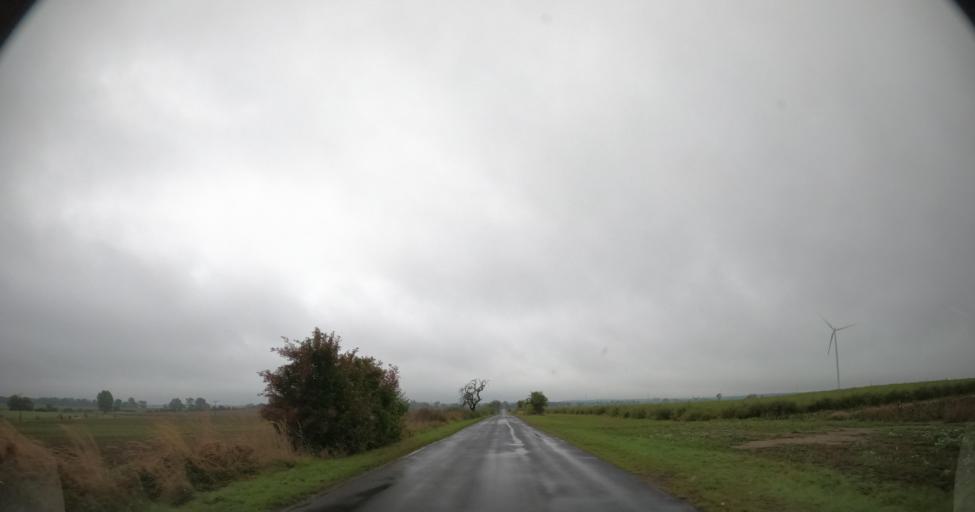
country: PL
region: West Pomeranian Voivodeship
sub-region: Powiat pyrzycki
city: Kozielice
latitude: 53.0594
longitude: 14.7807
